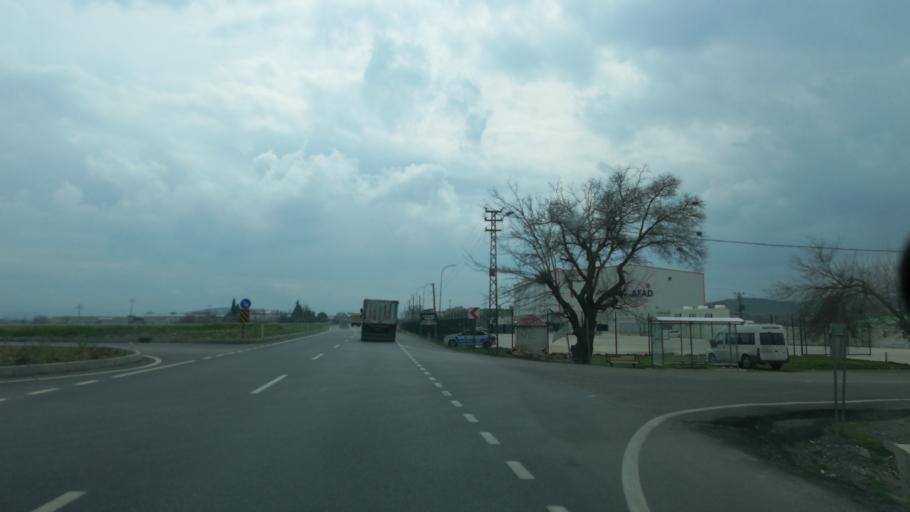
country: TR
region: Kahramanmaras
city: Turkoglu
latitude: 37.4505
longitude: 36.8880
